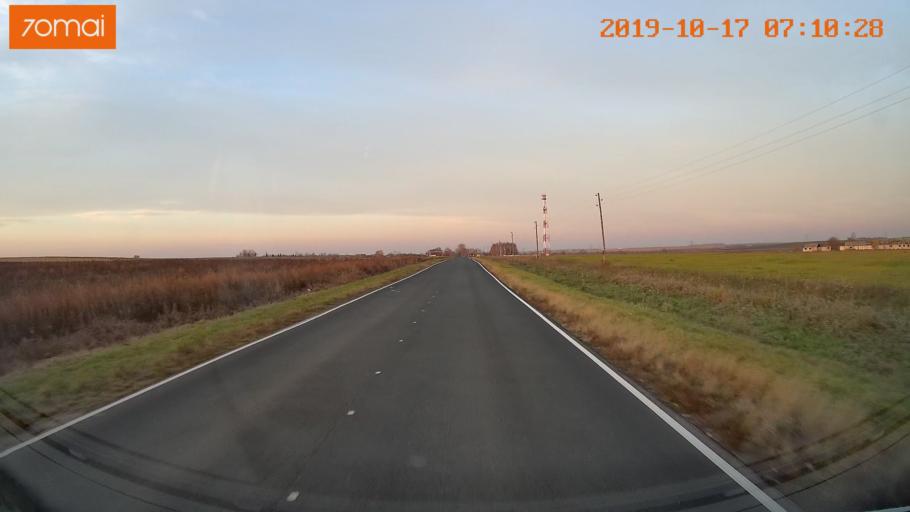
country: RU
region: Vladimir
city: Suzdal'
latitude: 56.4117
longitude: 40.3606
